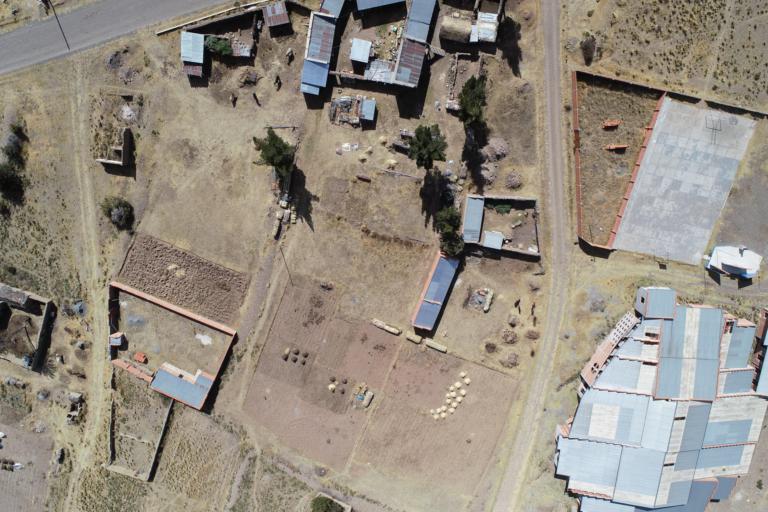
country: BO
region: La Paz
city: Achacachi
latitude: -15.8977
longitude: -68.9088
